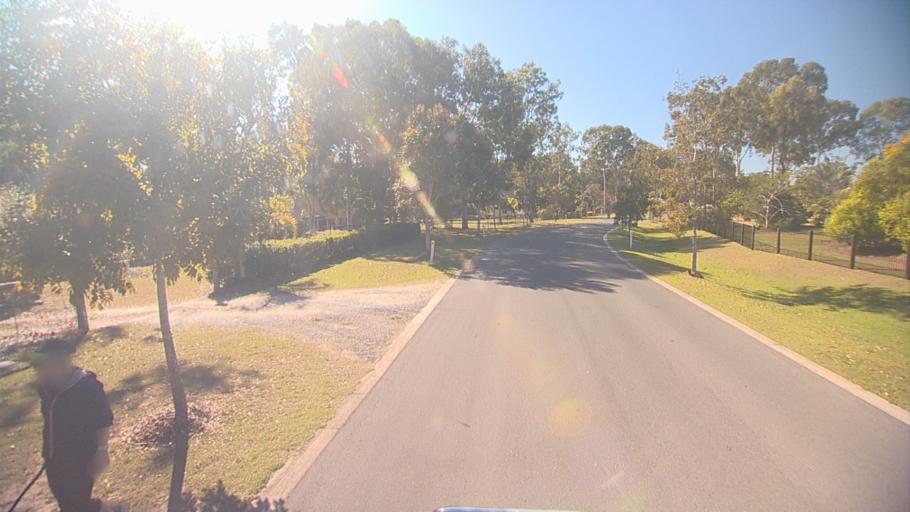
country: AU
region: Queensland
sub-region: Logan
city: North Maclean
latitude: -27.7461
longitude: 152.9500
